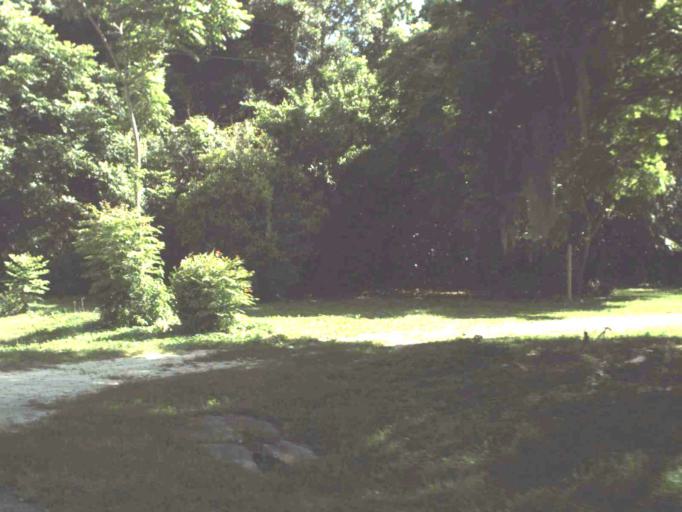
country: US
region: Florida
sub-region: Volusia County
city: Lake Helen
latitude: 29.0201
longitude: -81.2522
